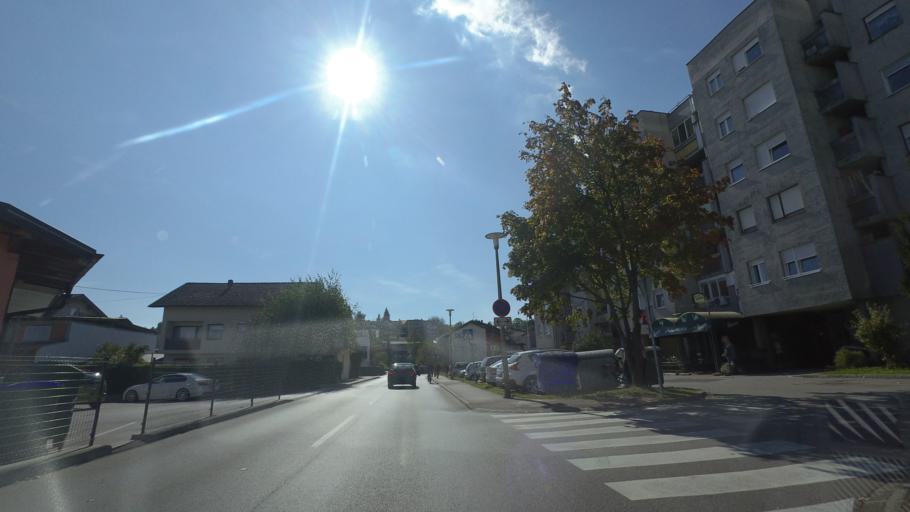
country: HR
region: Karlovacka
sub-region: Grad Karlovac
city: Karlovac
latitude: 45.4806
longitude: 15.5449
